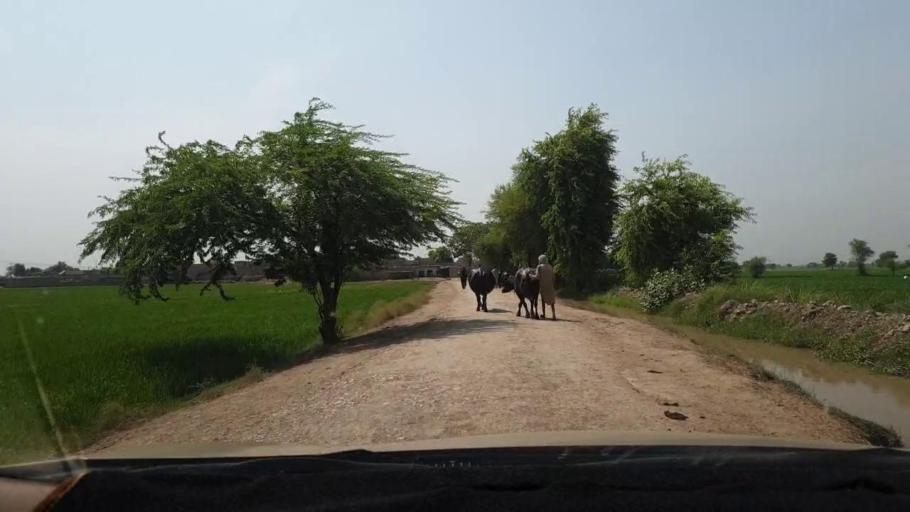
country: PK
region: Sindh
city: Naudero
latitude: 27.6497
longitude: 68.2604
